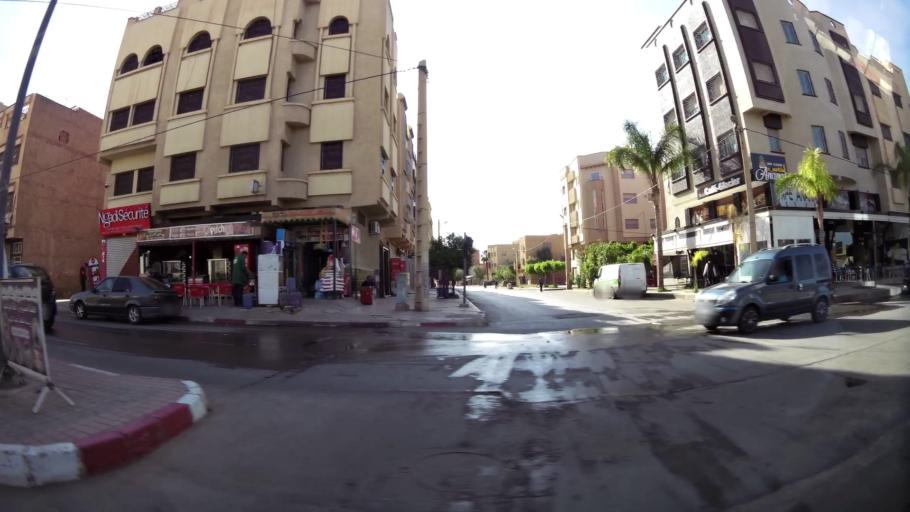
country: MA
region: Oriental
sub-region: Oujda-Angad
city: Oujda
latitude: 34.6698
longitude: -1.8947
